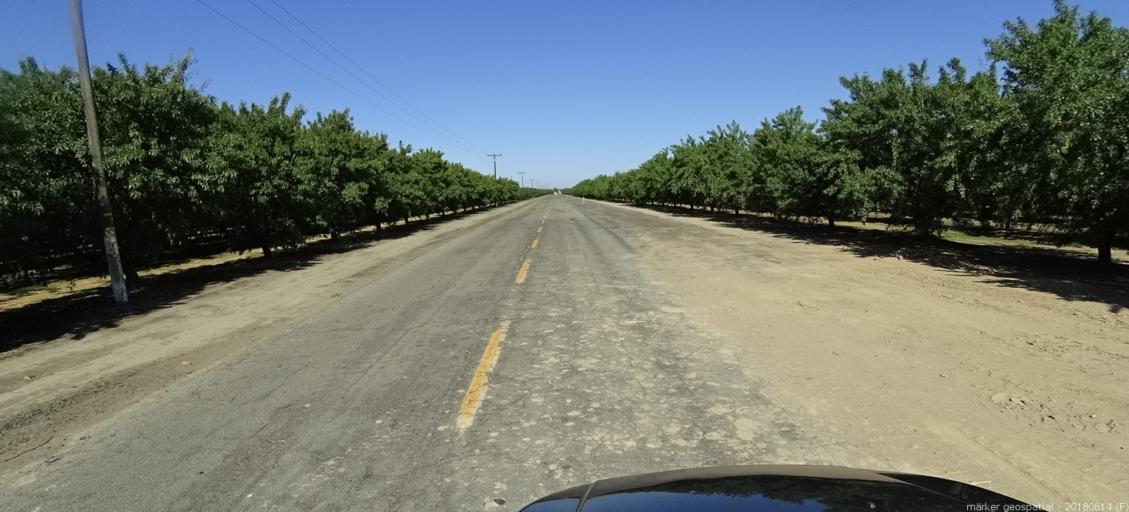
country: US
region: California
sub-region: Madera County
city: Madera Acres
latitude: 36.9819
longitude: -120.1576
